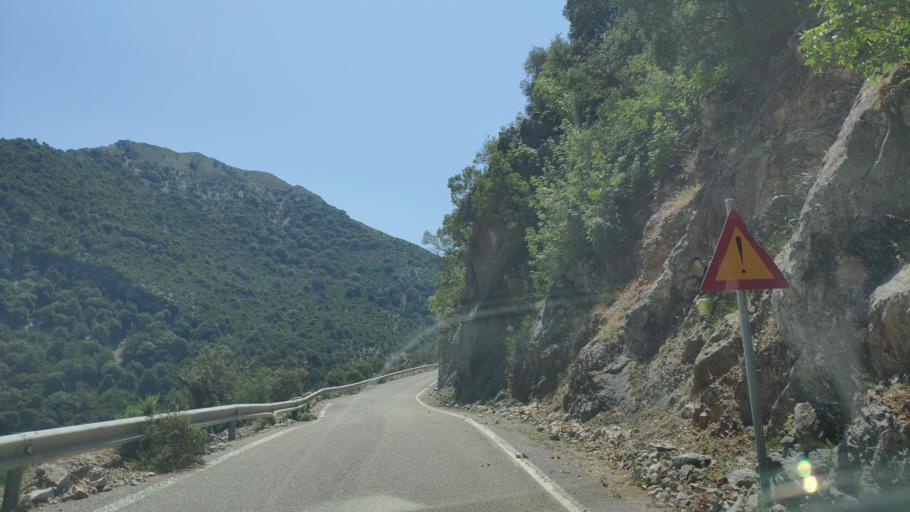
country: GR
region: West Greece
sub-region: Nomos Aitolias kai Akarnanias
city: Krikellos
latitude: 39.0173
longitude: 21.3529
